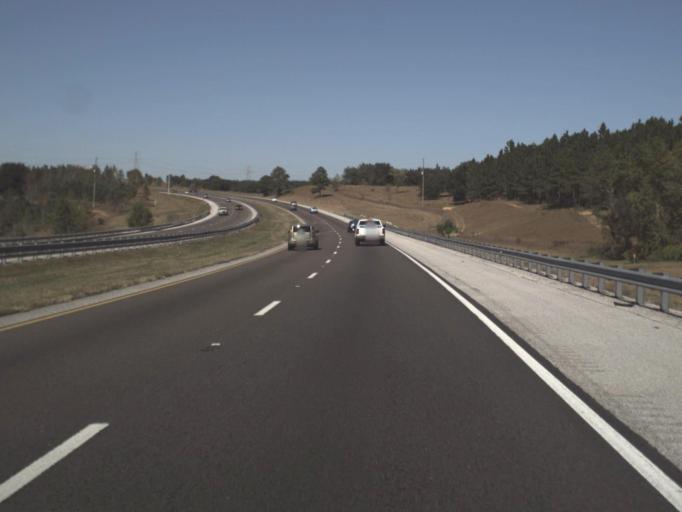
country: US
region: Florida
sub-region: Lake County
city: Minneola
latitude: 28.6073
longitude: -81.7256
